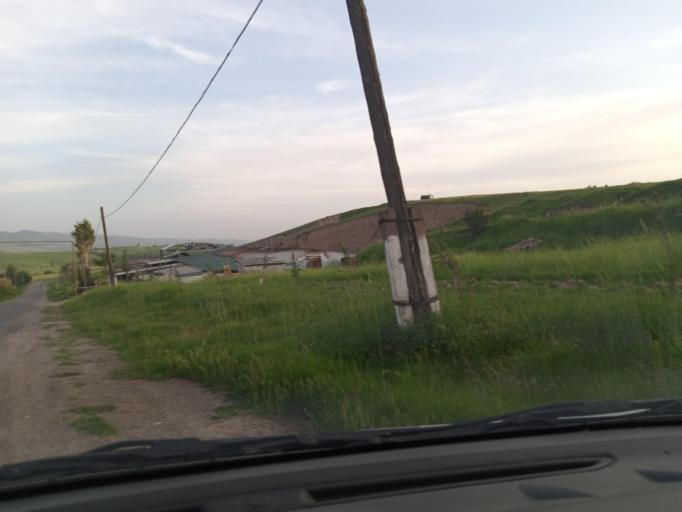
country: UZ
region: Toshkent
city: Parkent
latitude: 41.2336
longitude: 69.7374
